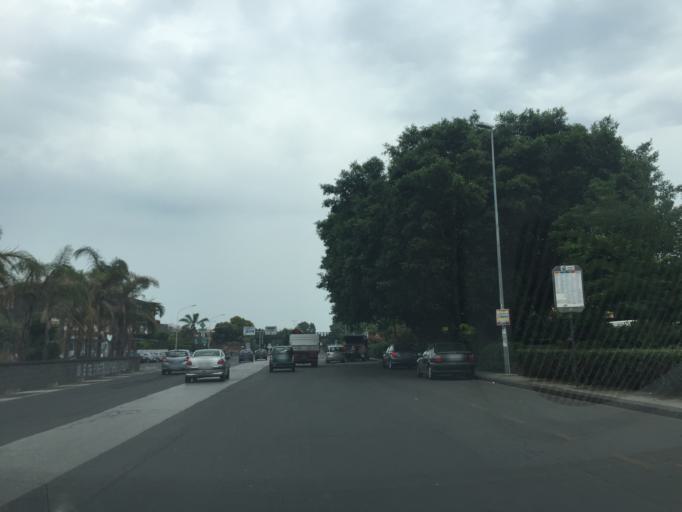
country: IT
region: Sicily
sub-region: Catania
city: Cerza
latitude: 37.5336
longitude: 15.1169
